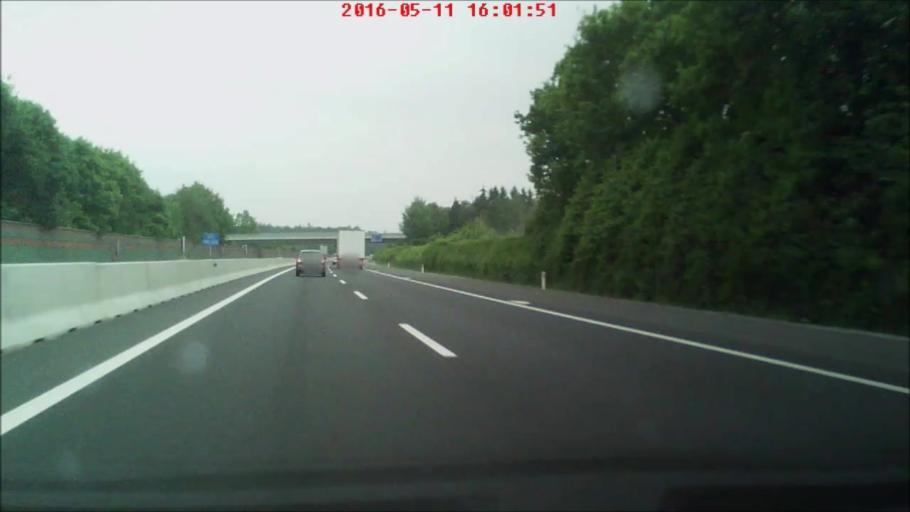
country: AT
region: Styria
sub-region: Politischer Bezirk Graz-Umgebung
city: Wundschuh
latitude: 46.9256
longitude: 15.4679
